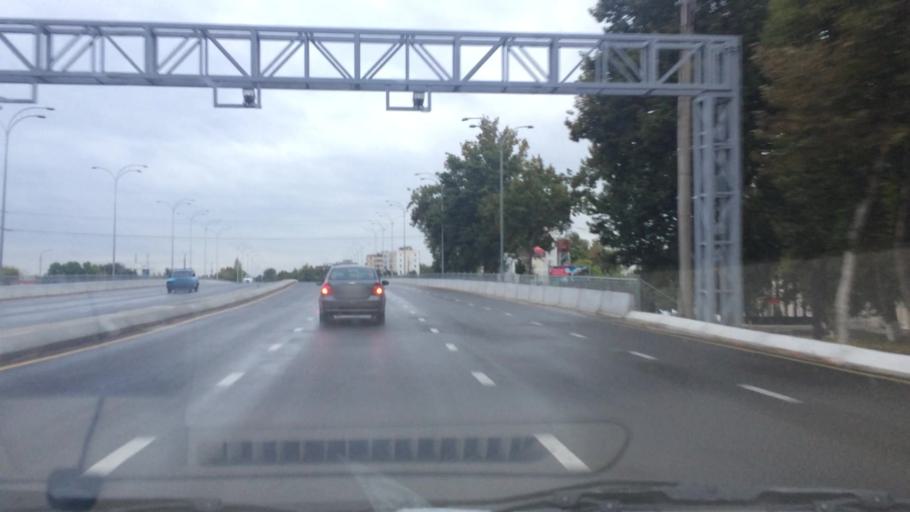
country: UZ
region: Toshkent Shahri
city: Tashkent
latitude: 41.2761
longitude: 69.2060
